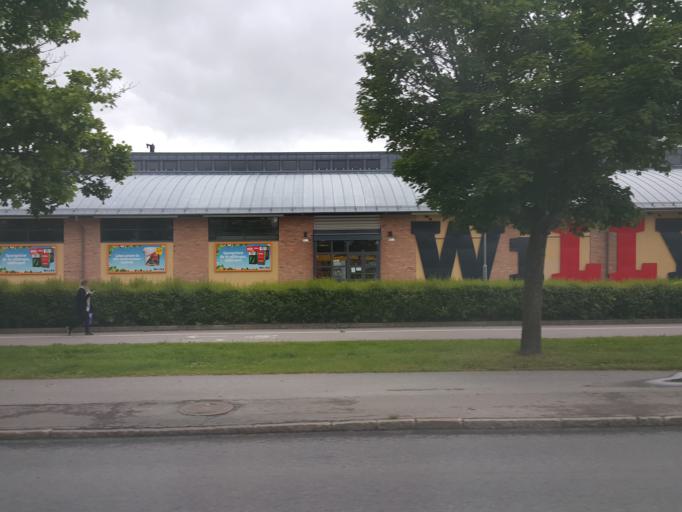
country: SE
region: Uppsala
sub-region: Uppsala Kommun
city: Uppsala
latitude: 59.8503
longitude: 17.6587
